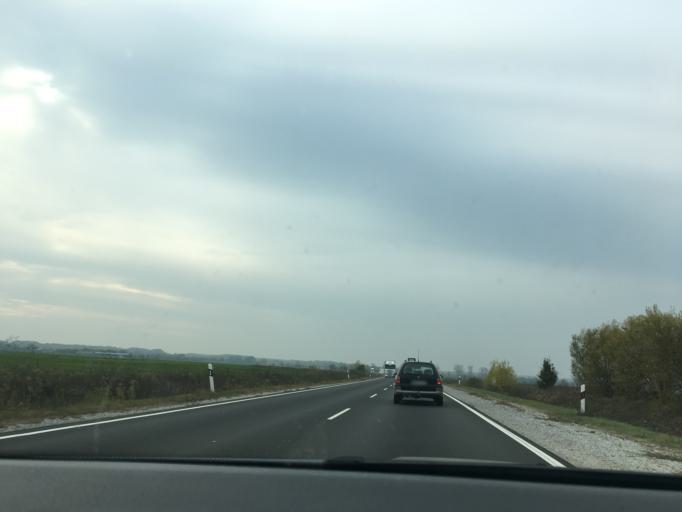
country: HU
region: Pest
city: Abony
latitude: 47.2204
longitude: 19.9945
